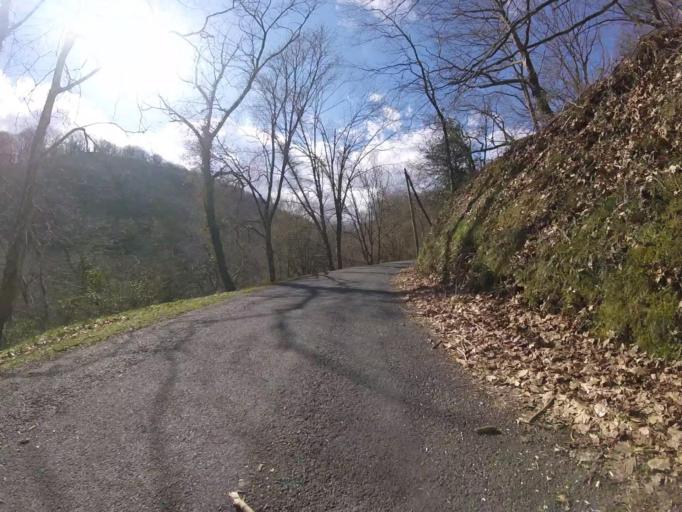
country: FR
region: Aquitaine
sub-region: Departement des Pyrenees-Atlantiques
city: Sare
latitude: 43.2705
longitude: -1.6041
